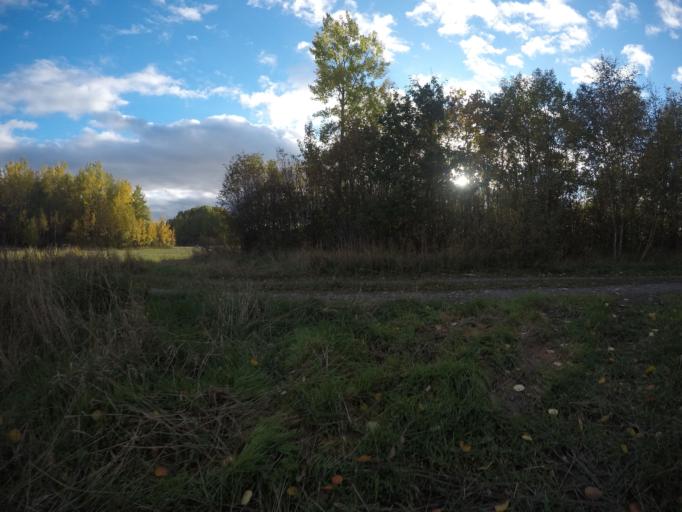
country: SE
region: Vaestmanland
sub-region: Arboga Kommun
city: Tyringe
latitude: 59.3046
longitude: 15.9880
